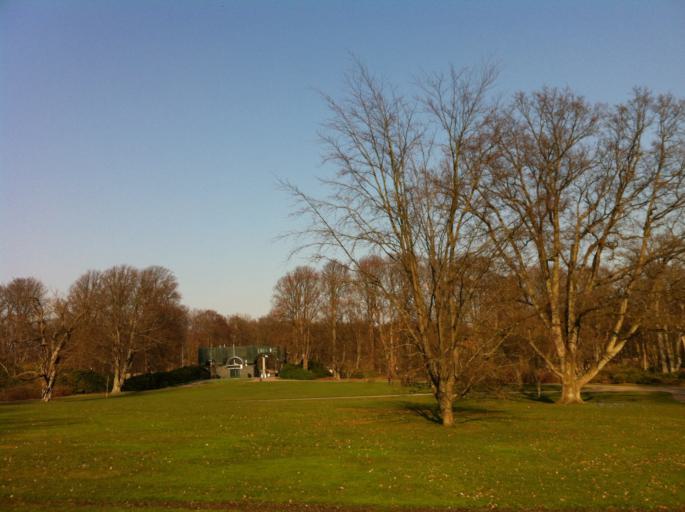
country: SE
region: Skane
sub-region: Helsingborg
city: Helsingborg
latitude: 56.0843
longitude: 12.6608
